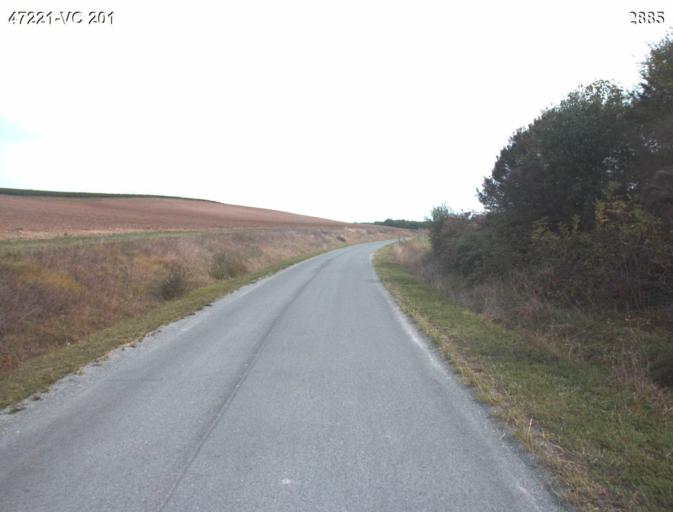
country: FR
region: Aquitaine
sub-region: Departement du Lot-et-Garonne
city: Mezin
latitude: 44.1093
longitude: 0.2534
